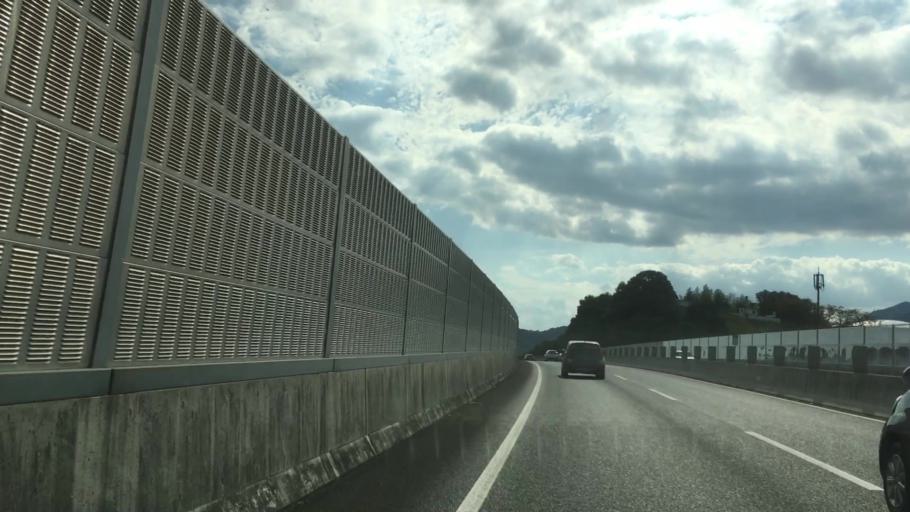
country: JP
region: Hiroshima
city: Hatsukaichi
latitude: 34.3557
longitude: 132.3233
